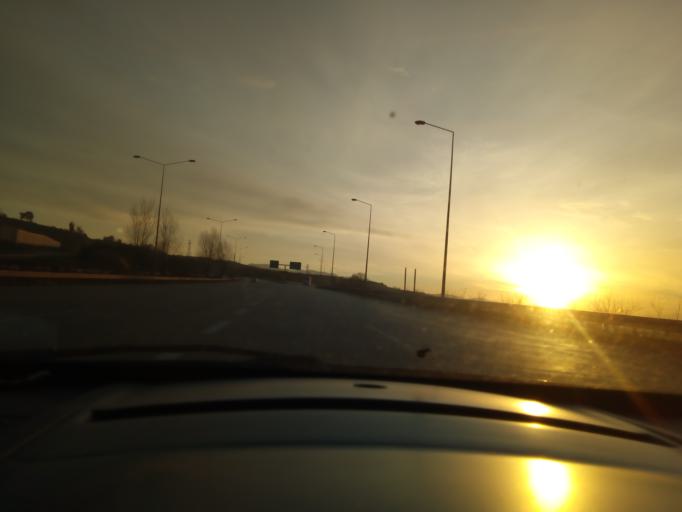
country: TR
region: Bursa
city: Niluefer
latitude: 40.2893
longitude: 29.0190
